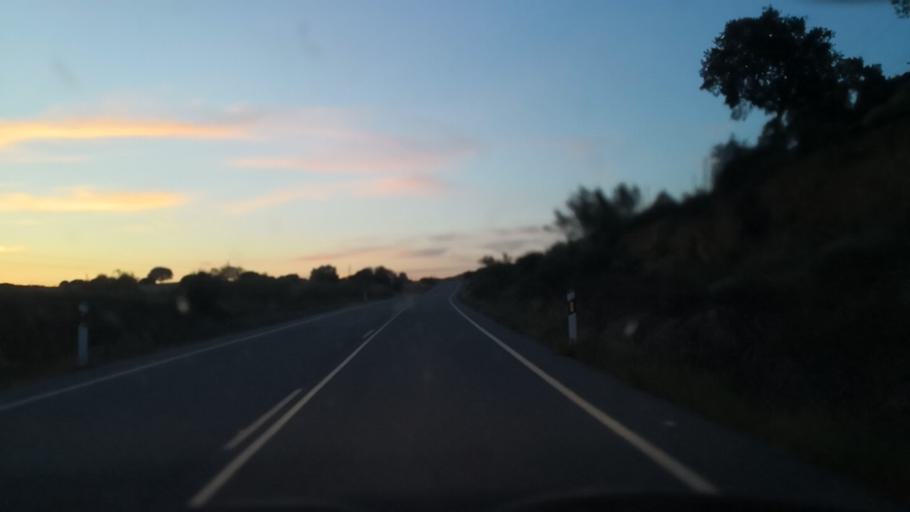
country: ES
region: Extremadura
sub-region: Provincia de Caceres
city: Piedras Albas
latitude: 39.7722
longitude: -6.9165
